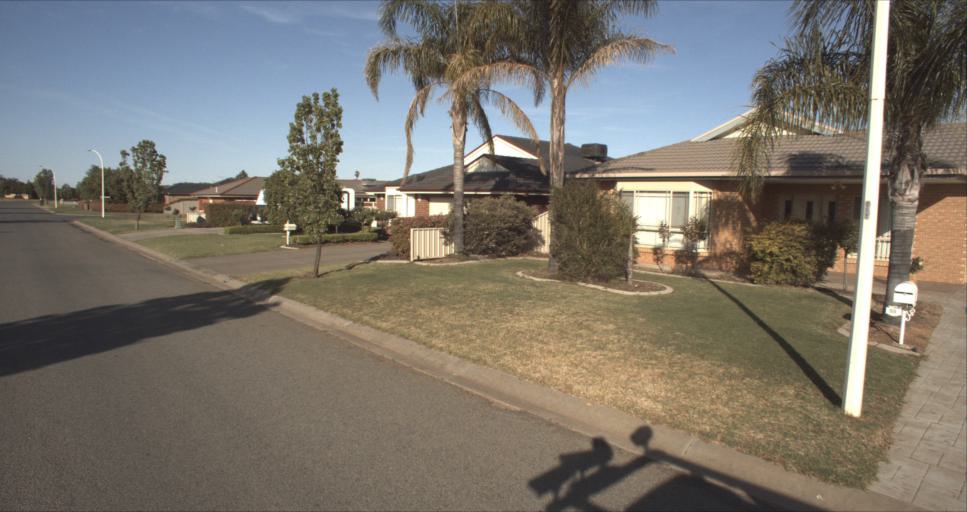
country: AU
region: New South Wales
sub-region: Leeton
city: Leeton
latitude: -34.5402
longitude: 146.4017
